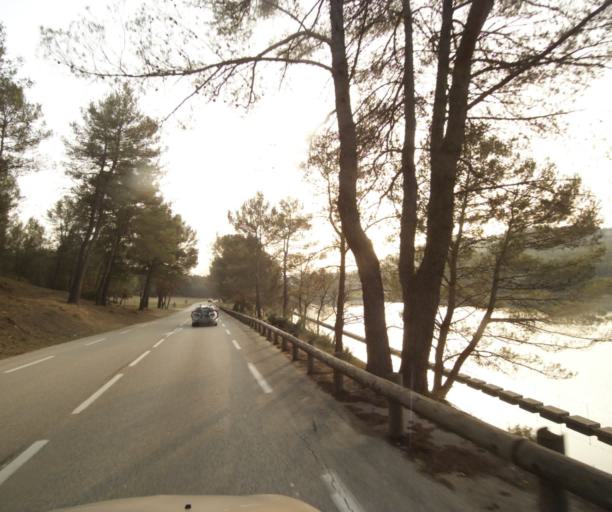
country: FR
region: Provence-Alpes-Cote d'Azur
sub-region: Departement du Vaucluse
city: Cadenet
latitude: 43.7050
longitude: 5.3518
